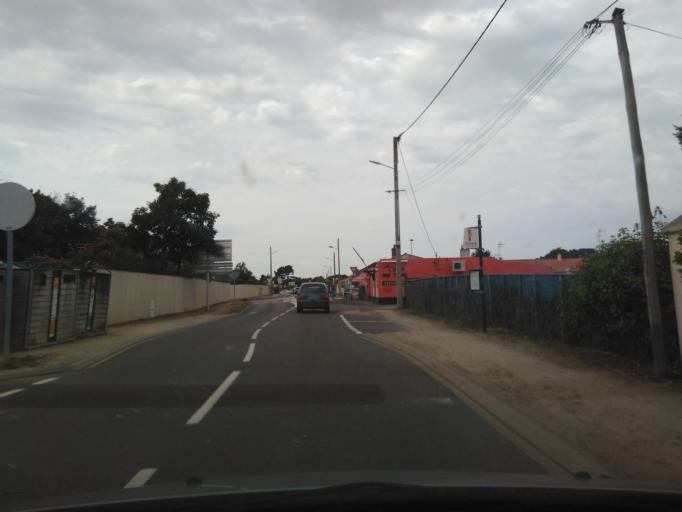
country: FR
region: Pays de la Loire
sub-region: Departement de la Vendee
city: Olonne-sur-Mer
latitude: 46.5458
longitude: -1.8035
